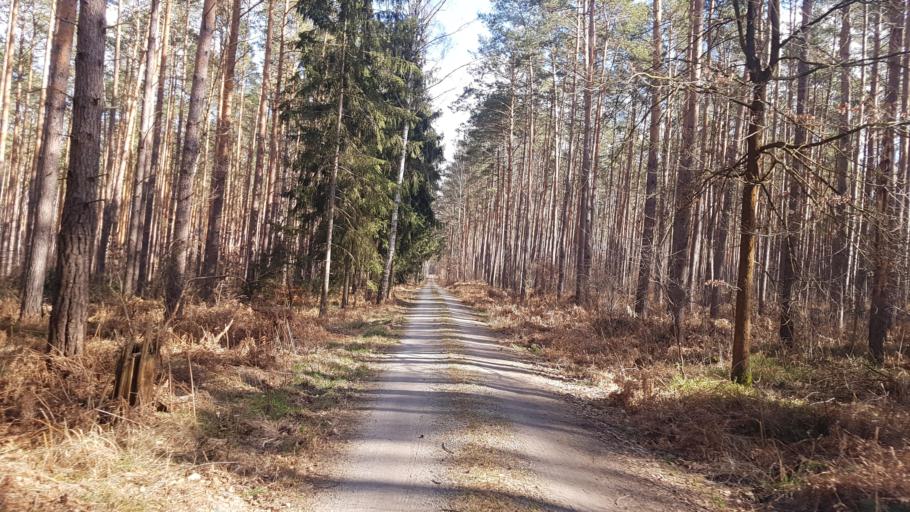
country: DE
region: Brandenburg
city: Plessa
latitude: 51.5165
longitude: 13.6070
